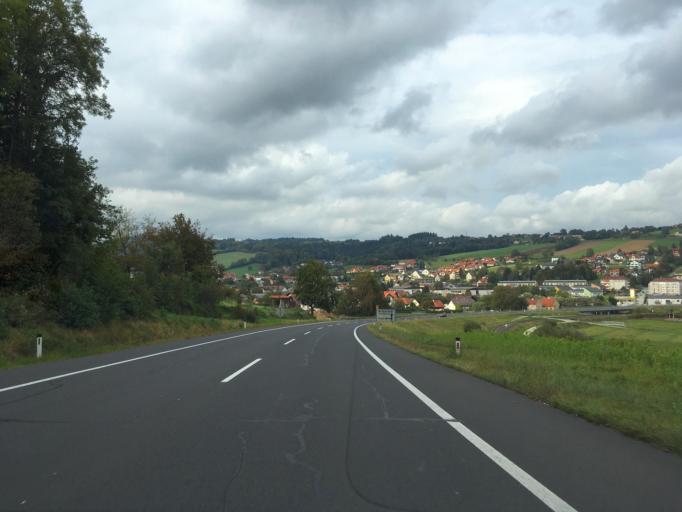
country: AT
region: Styria
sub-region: Politischer Bezirk Hartberg-Fuerstenfeld
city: Pinggau
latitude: 47.4352
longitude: 16.0656
